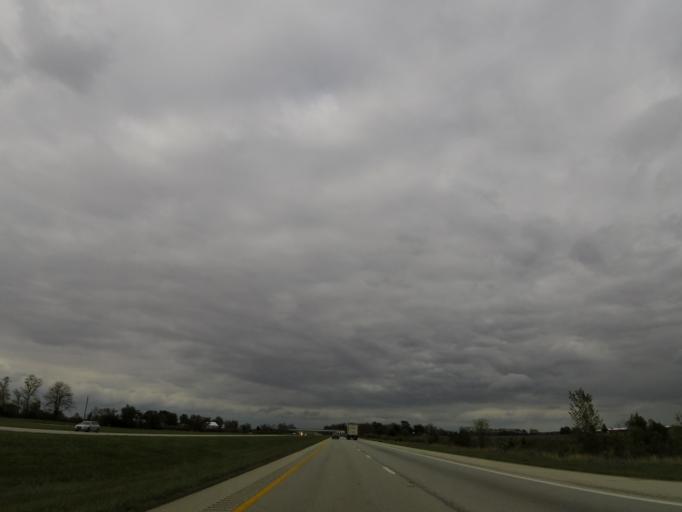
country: US
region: Ohio
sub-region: Clinton County
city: Wilmington
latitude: 39.5327
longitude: -83.7960
